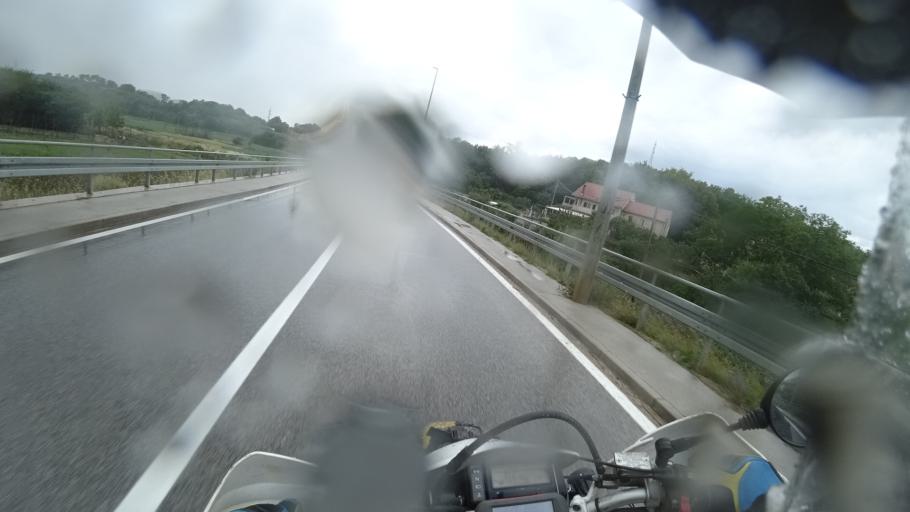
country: HR
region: Sibensko-Kniniska
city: Knin
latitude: 44.0450
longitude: 16.2145
